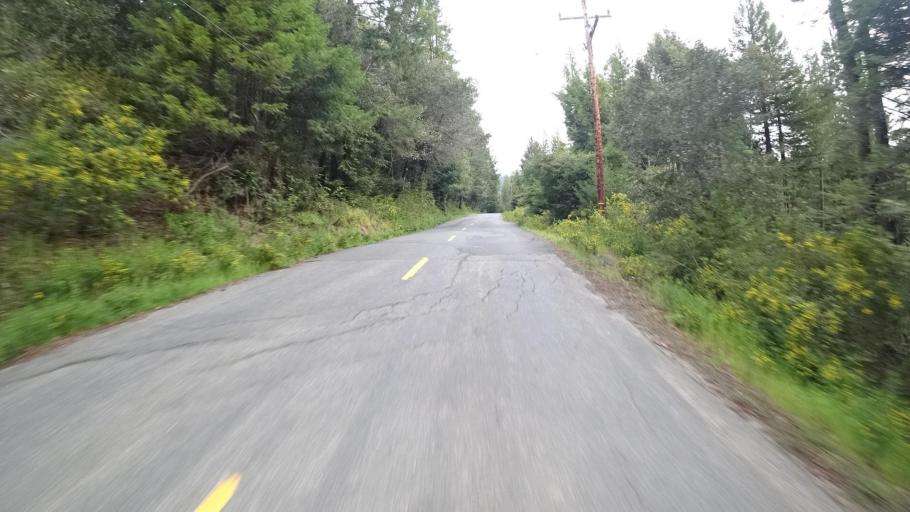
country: US
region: California
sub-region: Humboldt County
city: Redway
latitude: 40.2866
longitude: -123.8364
